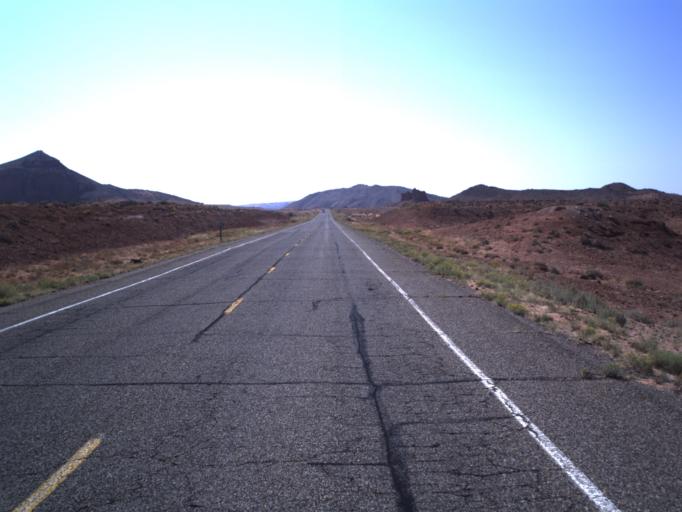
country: US
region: Utah
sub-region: San Juan County
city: Blanding
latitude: 36.9968
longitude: -109.6087
